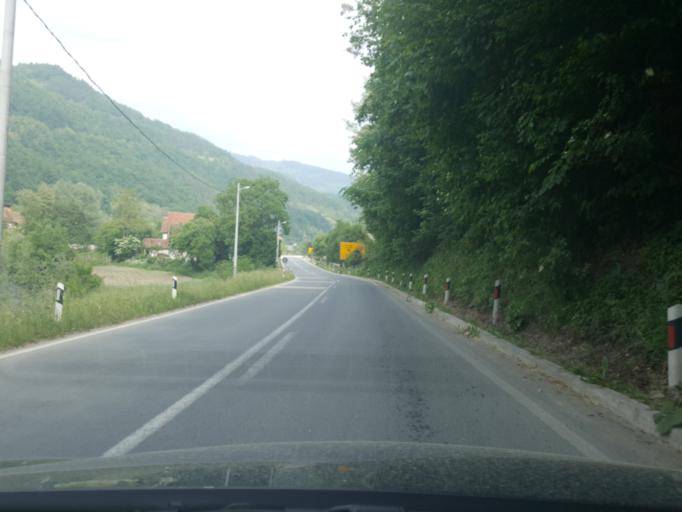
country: RS
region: Central Serbia
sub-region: Zlatiborski Okrug
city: Bajina Basta
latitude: 44.0395
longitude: 19.6220
